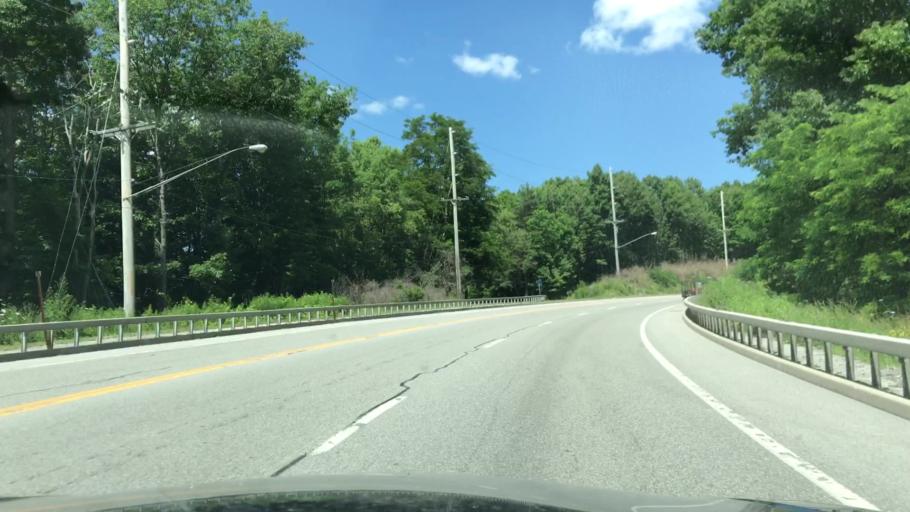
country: US
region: New York
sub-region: Wyoming County
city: Warsaw
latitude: 42.7454
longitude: -78.1269
